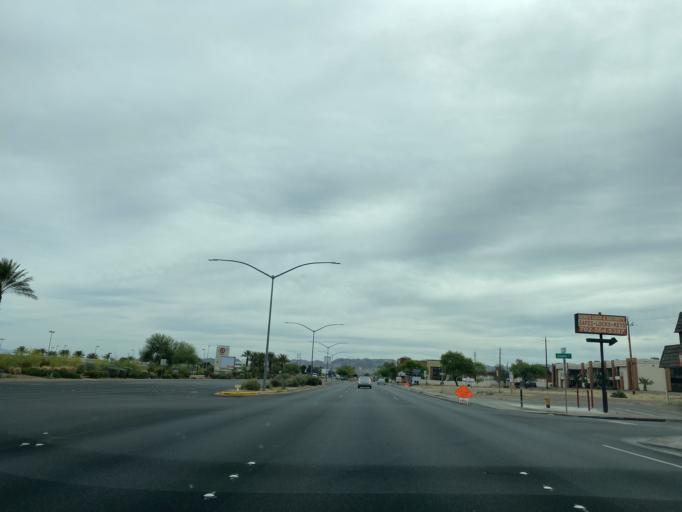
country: US
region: Nevada
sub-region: Clark County
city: Henderson
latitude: 36.0362
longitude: -114.9928
